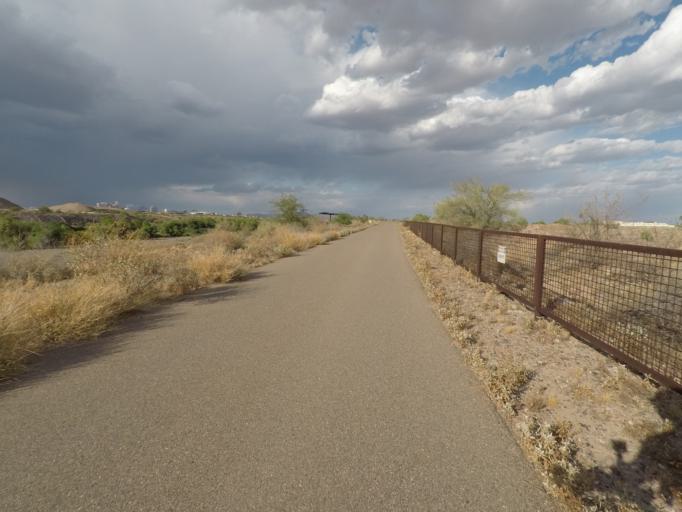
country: US
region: Arizona
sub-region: Maricopa County
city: Phoenix
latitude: 33.4139
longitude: -112.0891
